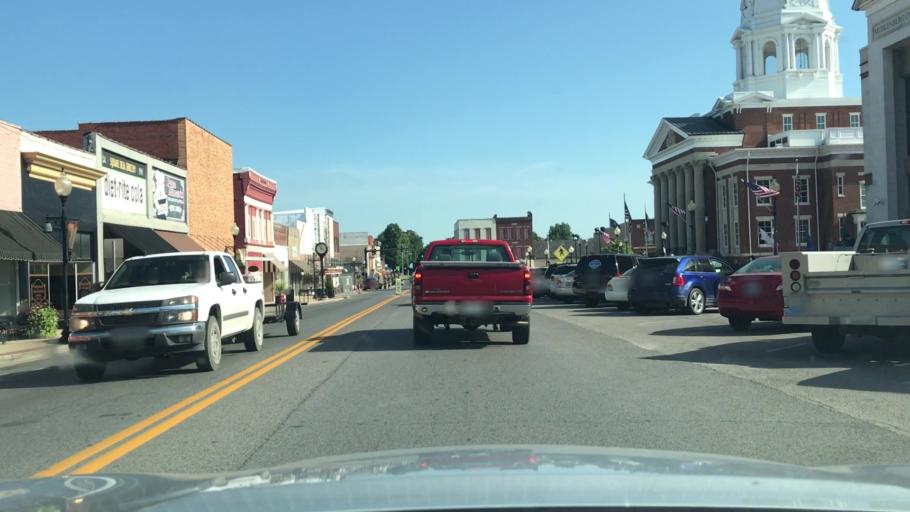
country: US
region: Kentucky
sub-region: Muhlenberg County
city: Greenville
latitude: 37.1997
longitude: -87.1783
